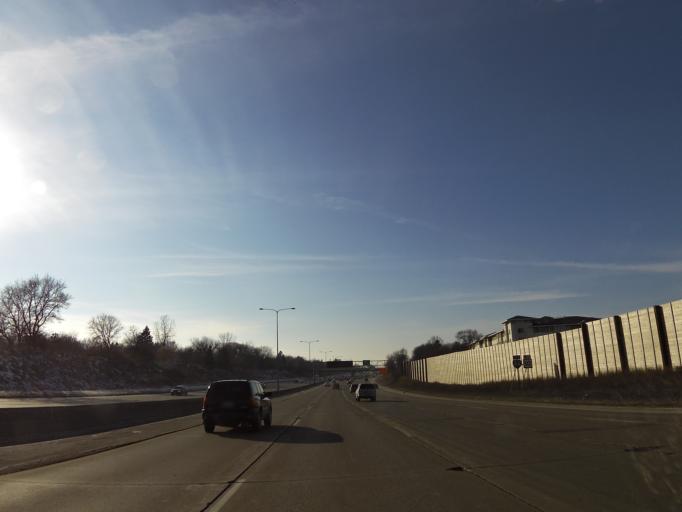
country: US
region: Minnesota
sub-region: Ramsey County
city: Saint Paul
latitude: 44.9521
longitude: -93.0501
